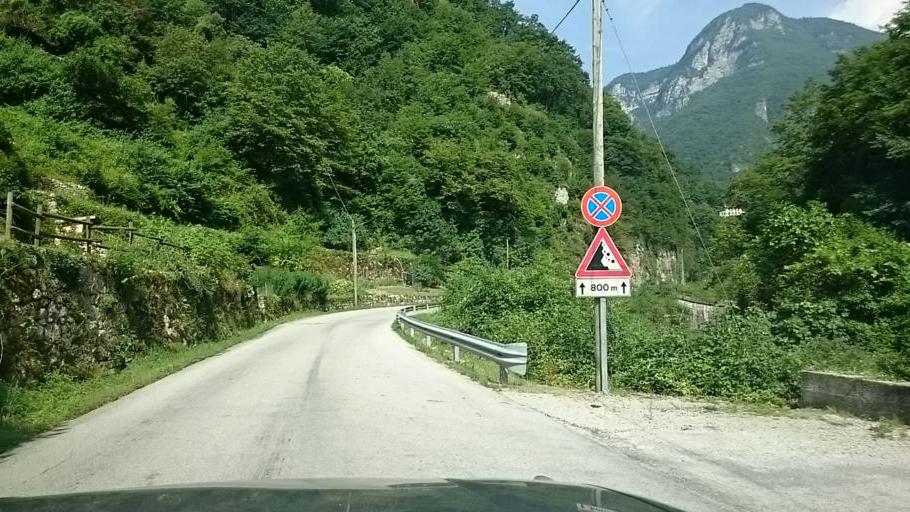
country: IT
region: Veneto
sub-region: Provincia di Vicenza
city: Valstagna
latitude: 45.8616
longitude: 11.6533
